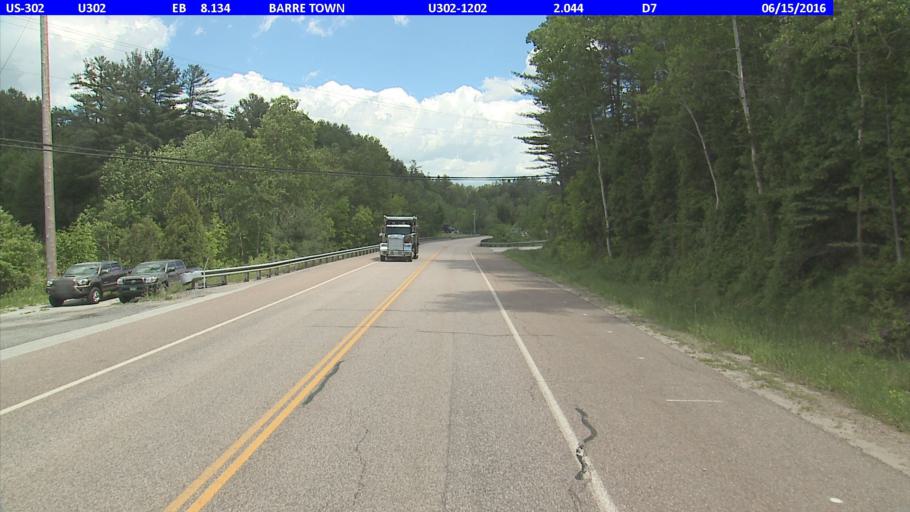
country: US
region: Vermont
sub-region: Washington County
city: South Barre
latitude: 44.1658
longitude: -72.4557
